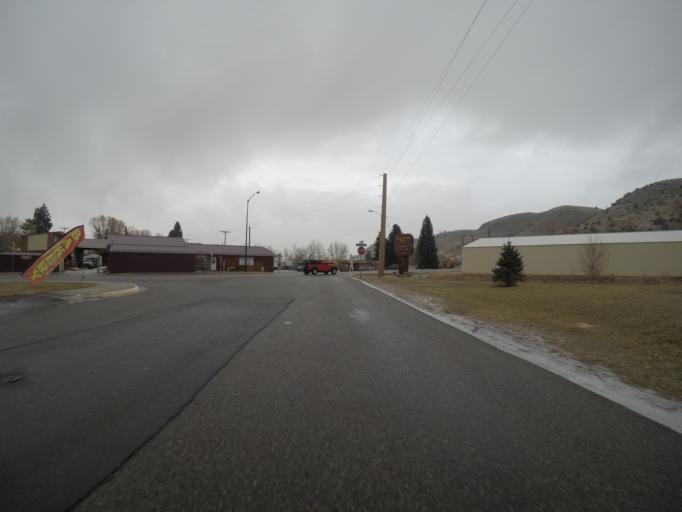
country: US
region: Montana
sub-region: Stillwater County
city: Absarokee
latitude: 45.5219
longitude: -109.4390
